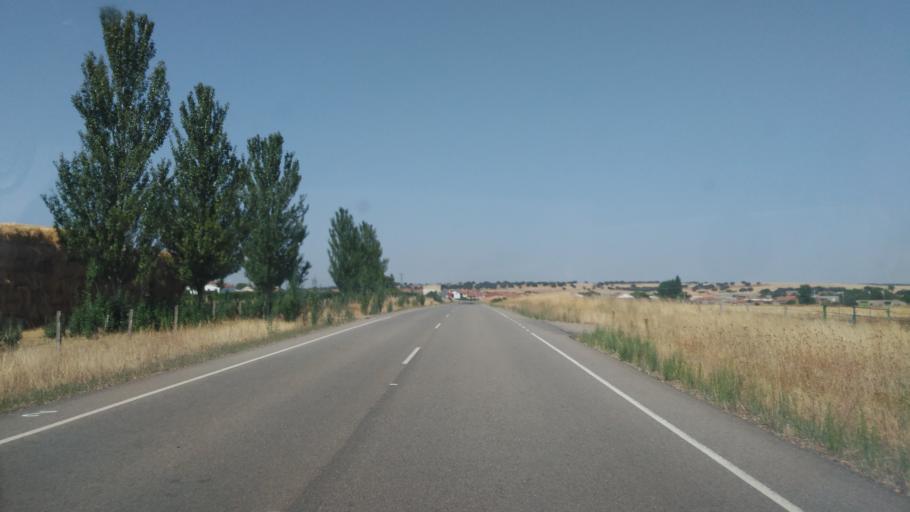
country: ES
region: Castille and Leon
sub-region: Provincia de Salamanca
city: Cabrillas
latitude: 40.7357
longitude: -6.1715
